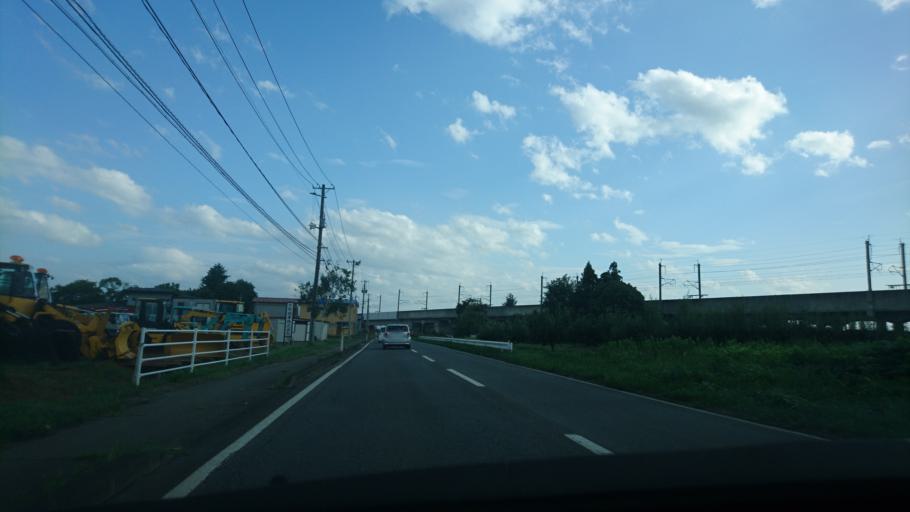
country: JP
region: Iwate
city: Mizusawa
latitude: 39.1750
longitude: 141.1774
